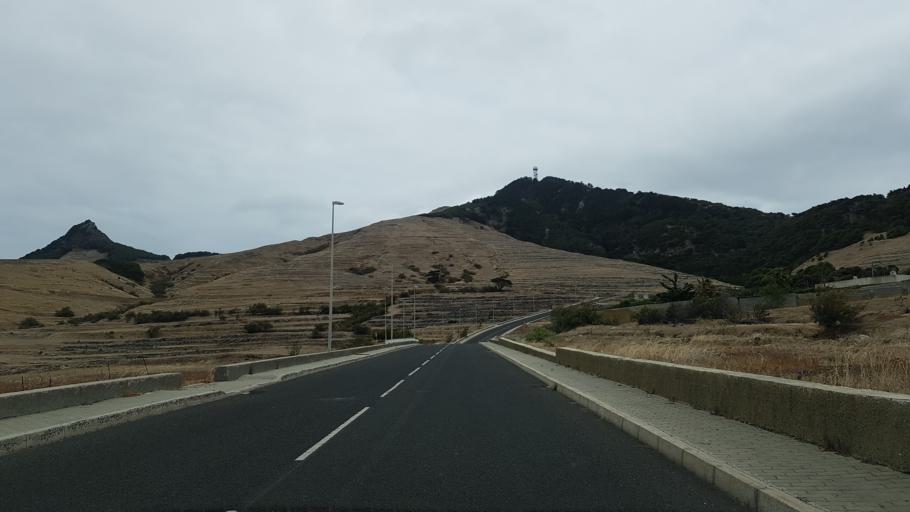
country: PT
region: Madeira
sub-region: Porto Santo
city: Camacha
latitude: 33.0890
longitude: -16.3382
